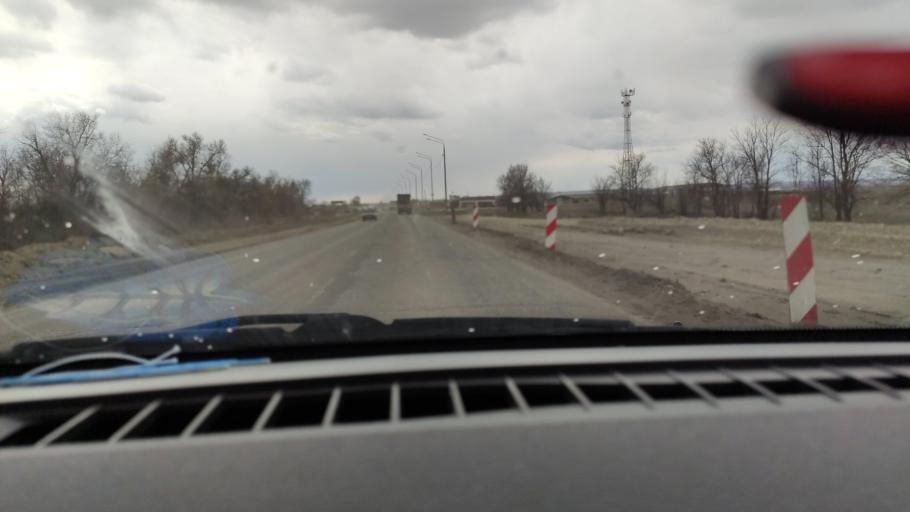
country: RU
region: Saratov
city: Sinodskoye
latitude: 51.9968
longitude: 46.6743
